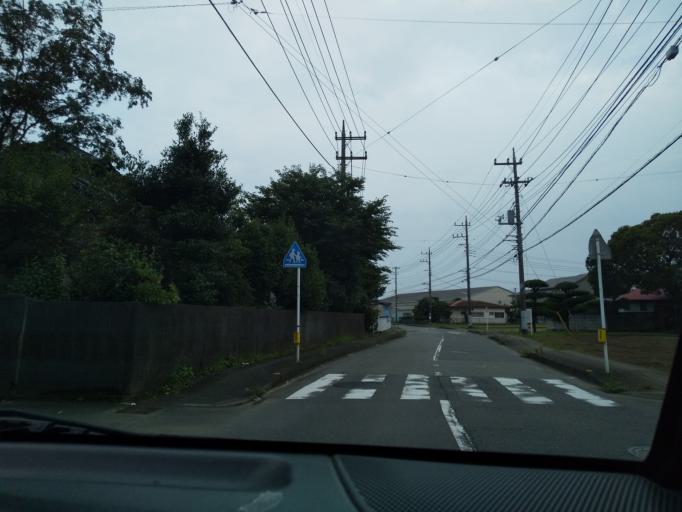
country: JP
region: Kanagawa
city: Atsugi
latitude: 35.4128
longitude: 139.3909
